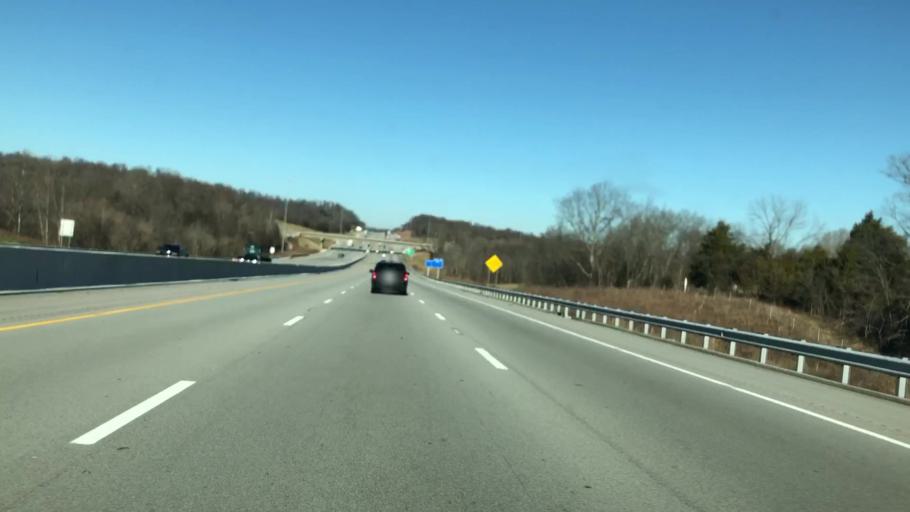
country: US
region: Kentucky
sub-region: Hart County
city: Munfordville
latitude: 37.3746
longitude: -85.8890
